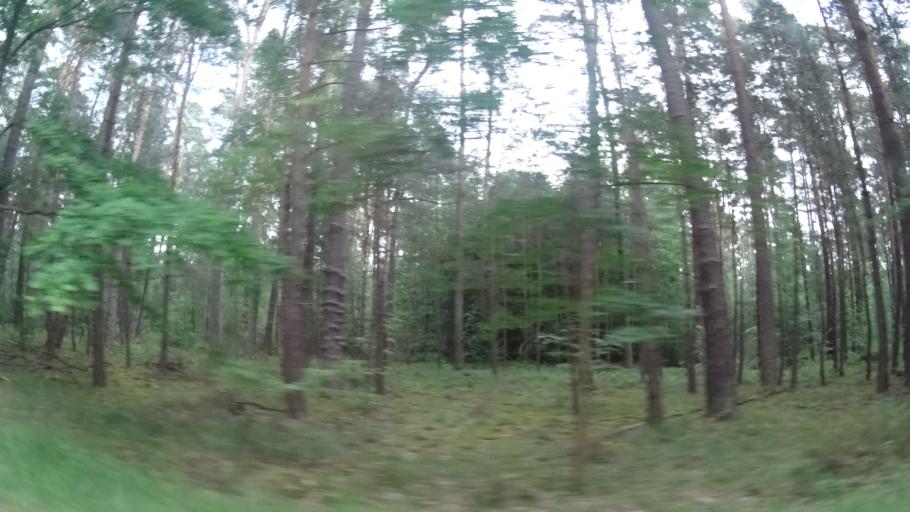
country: DE
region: Rheinland-Pfalz
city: Dudenhofen
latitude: 49.3335
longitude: 8.3744
